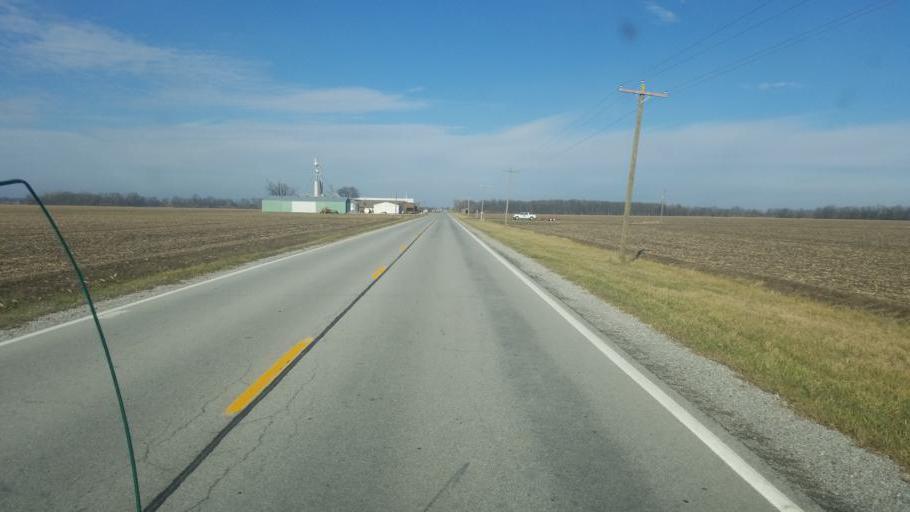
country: US
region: Illinois
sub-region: Saline County
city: Eldorado
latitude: 37.8691
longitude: -88.4529
